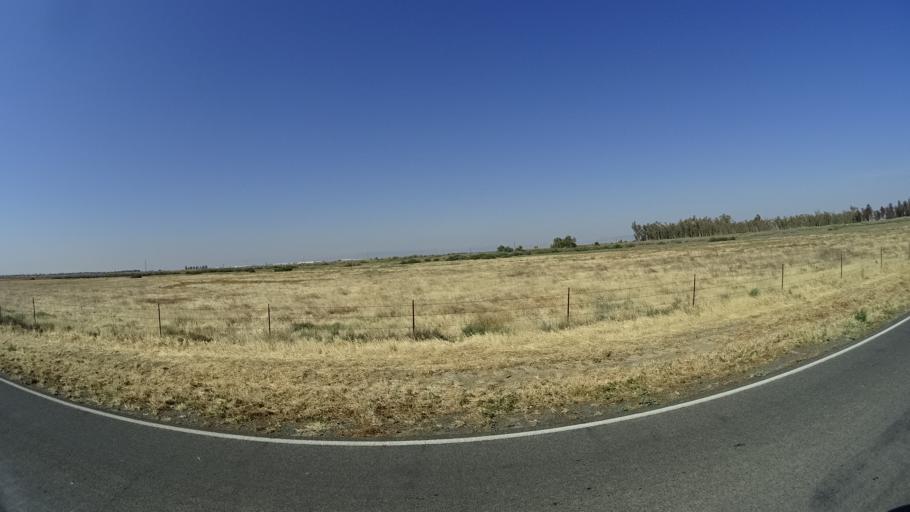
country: US
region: California
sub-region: Fresno County
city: Riverdale
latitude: 36.3741
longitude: -119.9263
